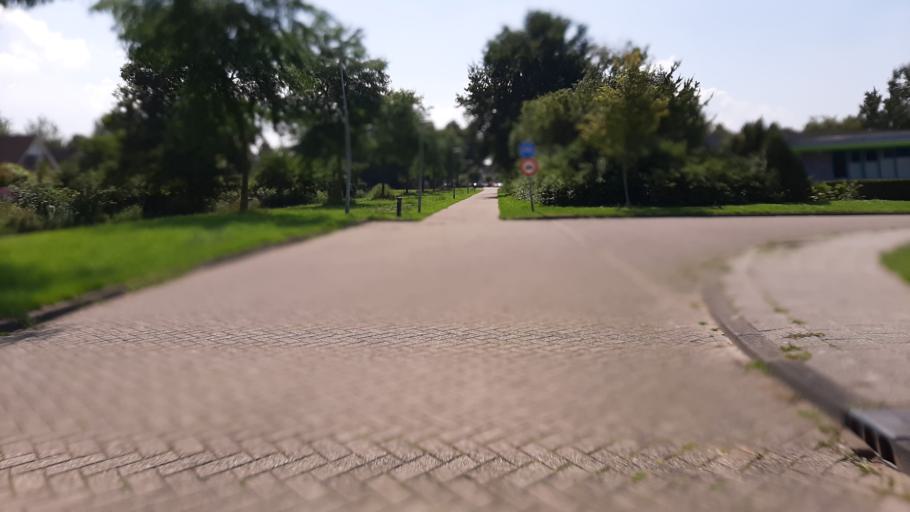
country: NL
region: Flevoland
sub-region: Gemeente Zeewolde
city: Zeewolde
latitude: 52.3242
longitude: 5.5337
